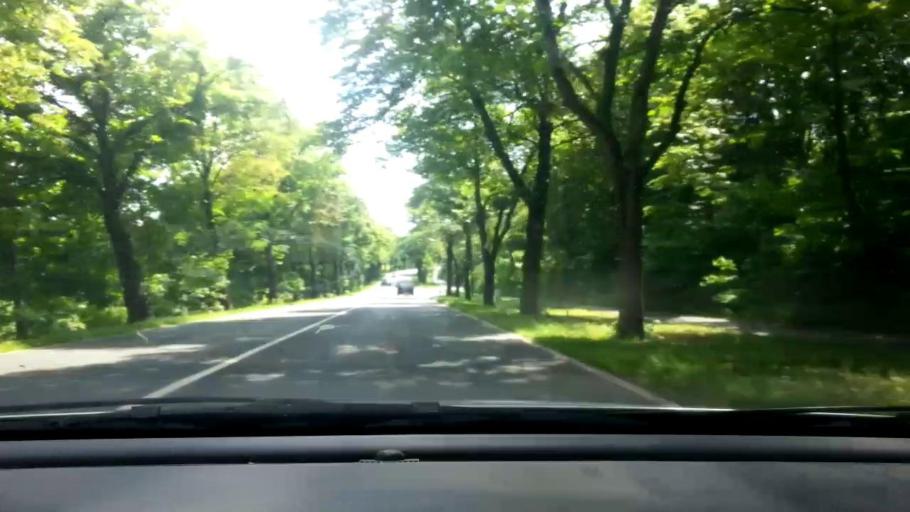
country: DE
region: Bavaria
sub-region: Upper Franconia
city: Bayreuth
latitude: 49.9382
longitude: 11.6130
